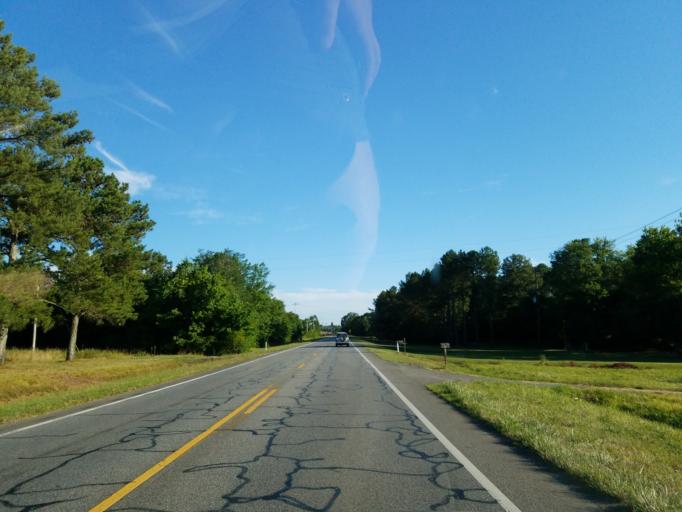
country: US
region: Georgia
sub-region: Bartow County
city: Adairsville
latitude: 34.4242
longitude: -84.9343
